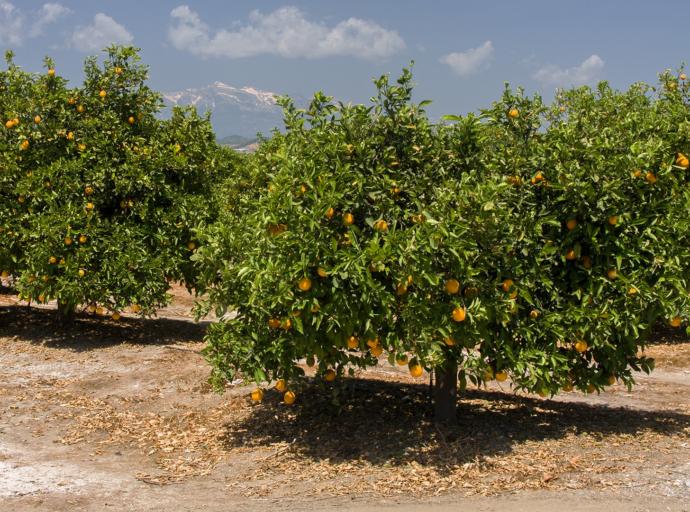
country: GR
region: Peloponnese
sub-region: Nomos Lakonias
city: Skala
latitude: 36.8252
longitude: 22.6451
